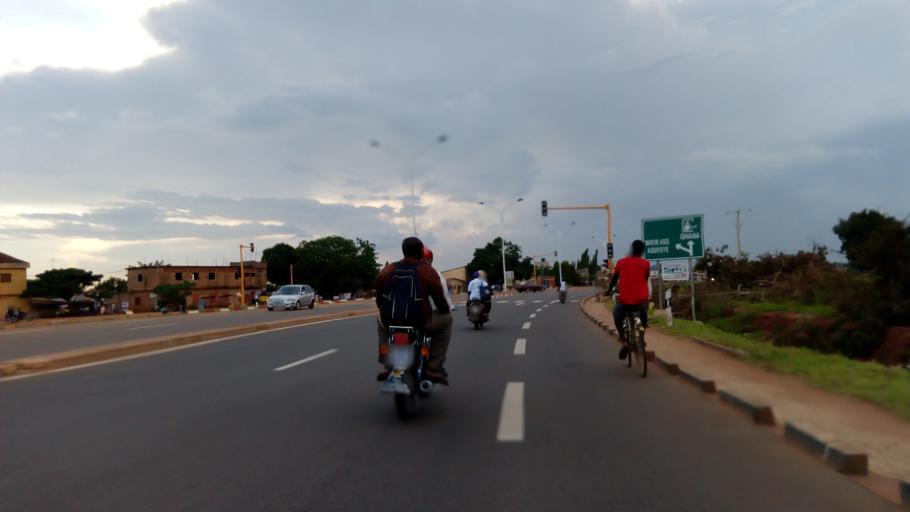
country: TG
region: Maritime
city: Lome
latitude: 6.2448
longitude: 1.1853
